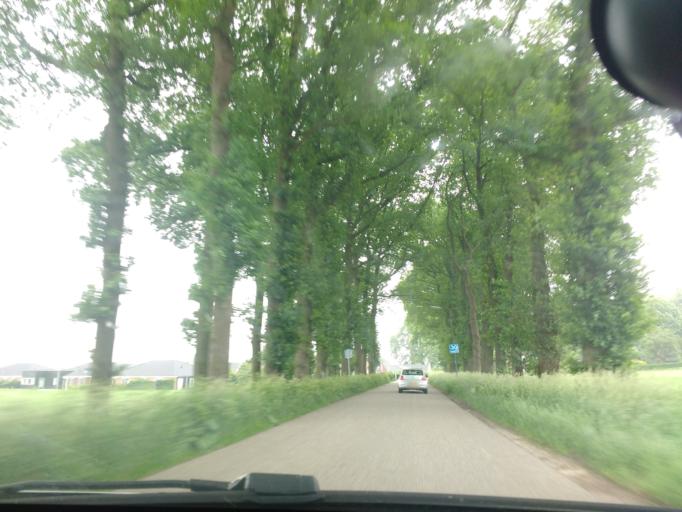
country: NL
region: Utrecht
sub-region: Gemeente Rhenen
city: Rhenen
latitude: 51.9601
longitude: 5.6049
